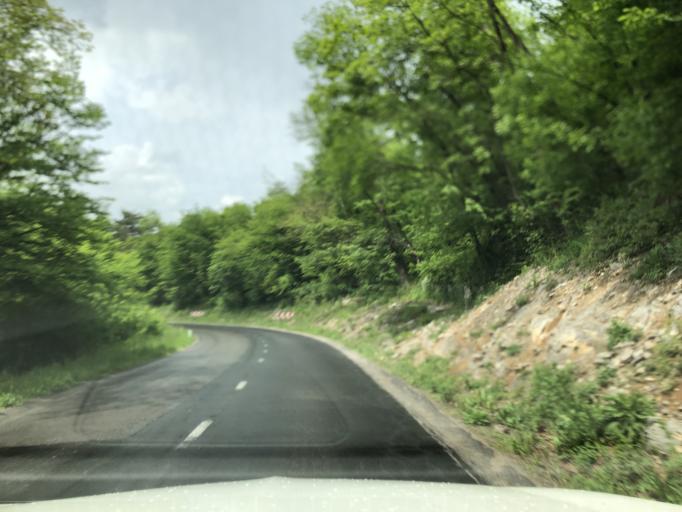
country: SI
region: Bloke
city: Nova Vas
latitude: 45.7640
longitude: 14.4361
